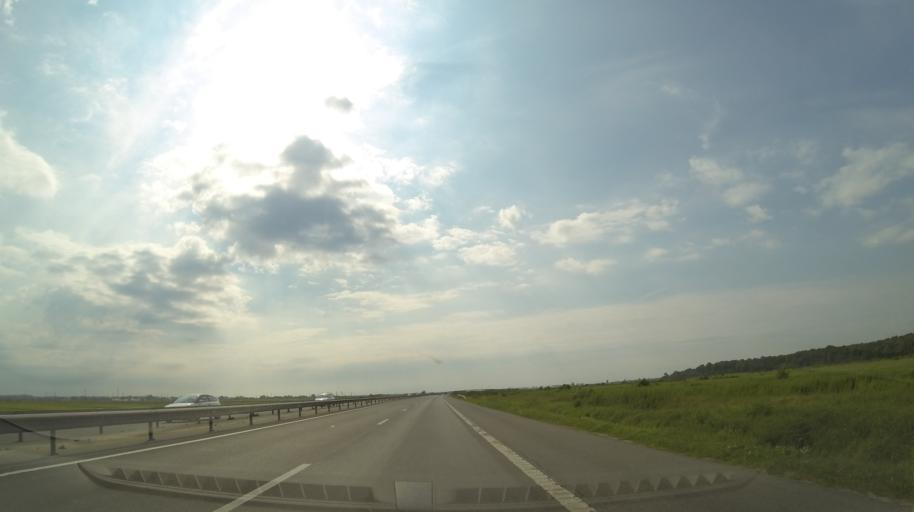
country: RO
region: Dambovita
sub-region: Comuna Corbii Mari
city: Ungureni
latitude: 44.5708
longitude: 25.4827
